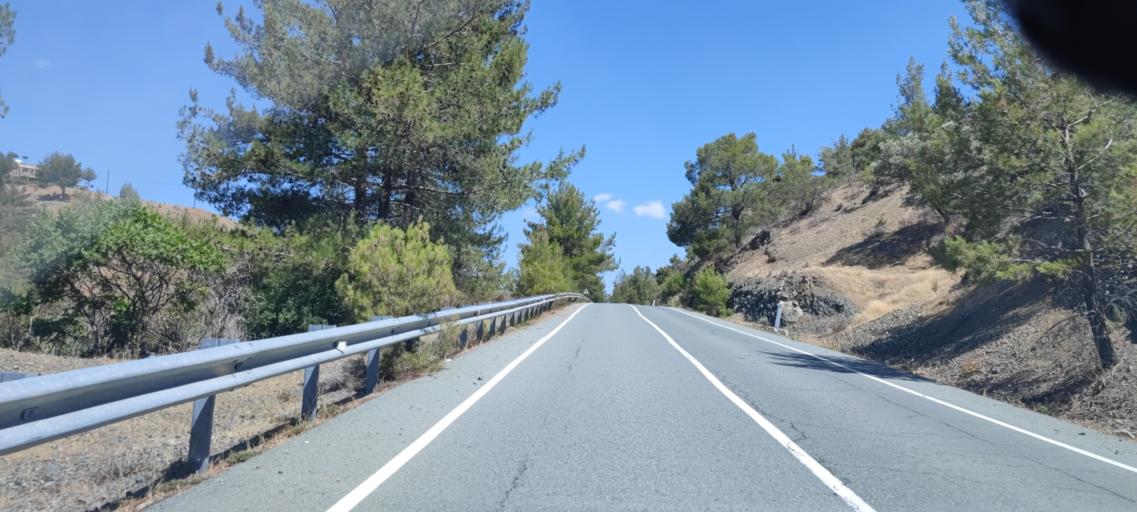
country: CY
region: Lefkosia
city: Kakopetria
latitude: 34.9152
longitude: 32.8149
